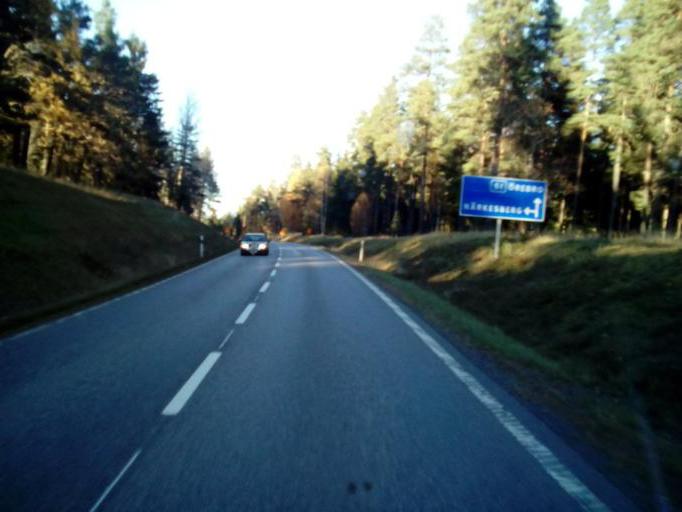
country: SE
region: OErebro
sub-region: Hallsbergs Kommun
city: Palsboda
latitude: 58.8990
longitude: 15.4348
